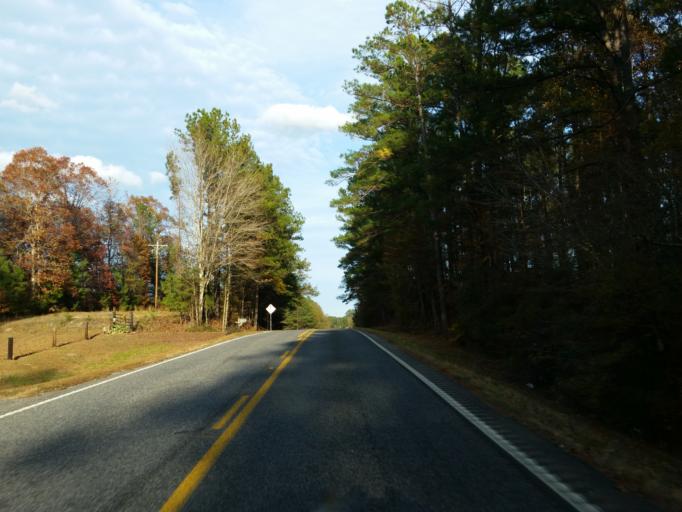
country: US
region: Mississippi
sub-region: Clarke County
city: Stonewall
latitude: 32.2147
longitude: -88.7849
